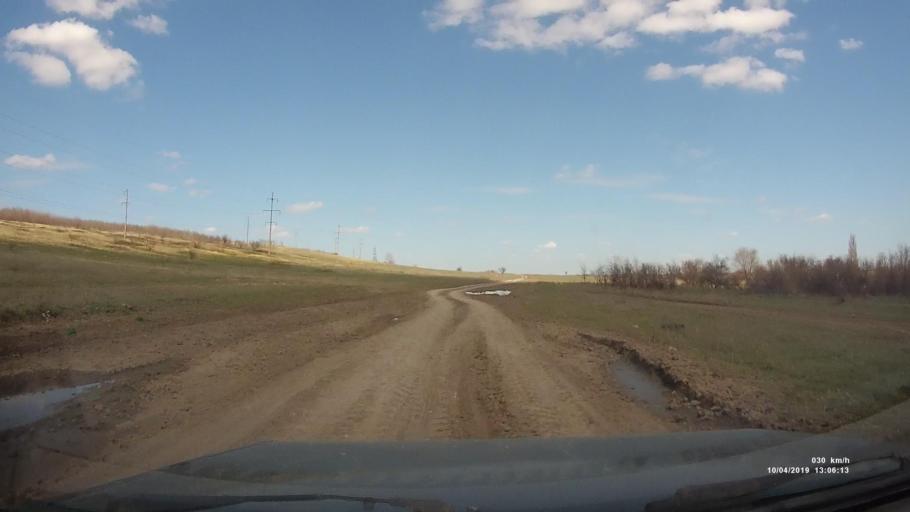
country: RU
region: Rostov
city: Masalovka
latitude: 48.3911
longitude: 40.2355
